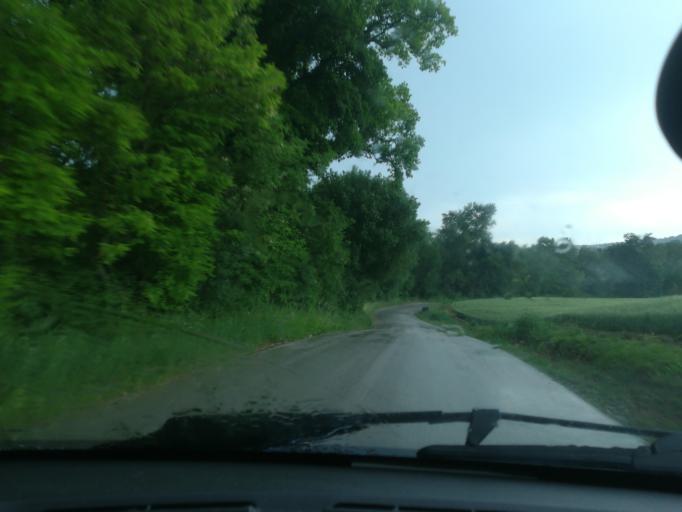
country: IT
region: The Marches
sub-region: Provincia di Macerata
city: Passo di Treia
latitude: 43.3005
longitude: 13.3459
